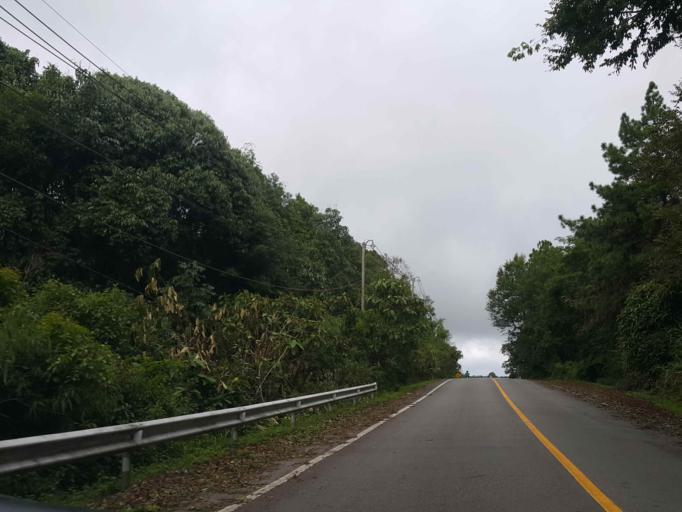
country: TH
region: Chiang Mai
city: Mae Chaem
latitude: 18.5334
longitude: 98.4945
